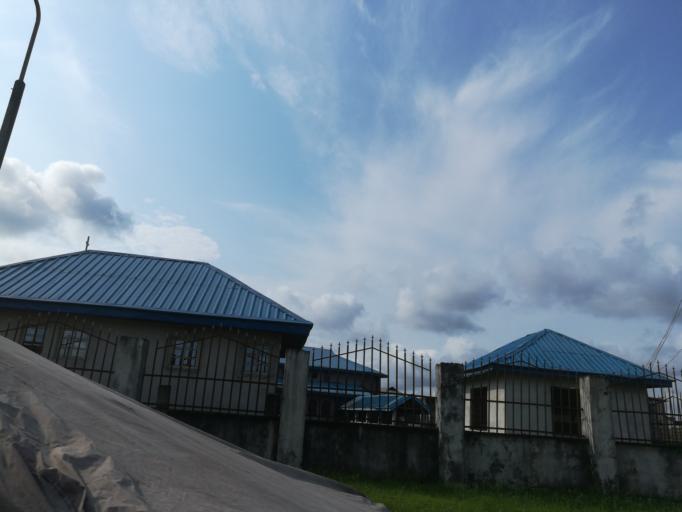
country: NG
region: Rivers
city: Okrika
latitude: 4.7421
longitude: 7.0790
